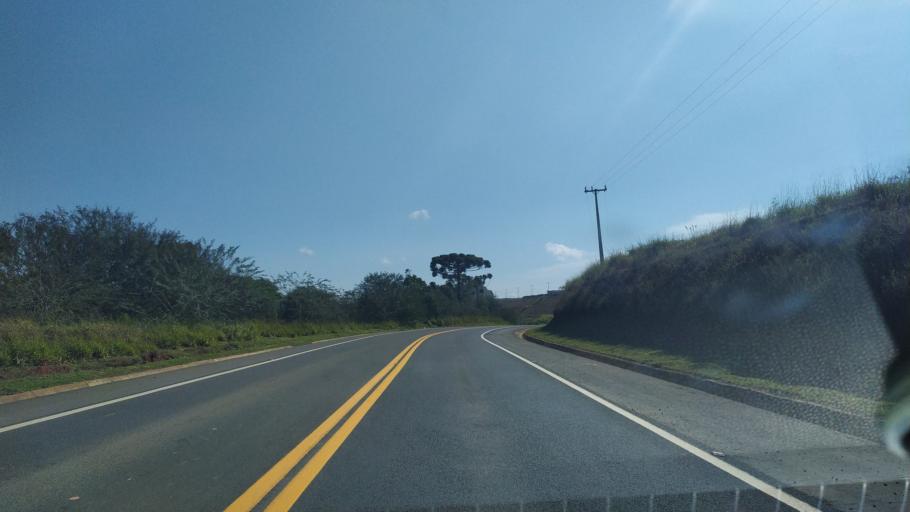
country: BR
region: Parana
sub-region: Telemaco Borba
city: Telemaco Borba
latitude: -24.2517
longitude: -50.7453
